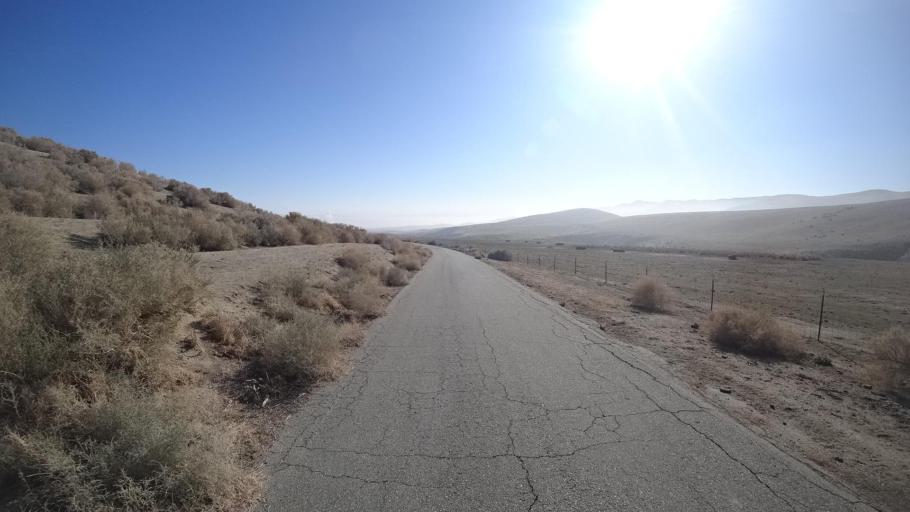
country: US
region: California
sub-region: Kern County
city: Taft Heights
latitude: 35.2328
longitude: -119.6545
